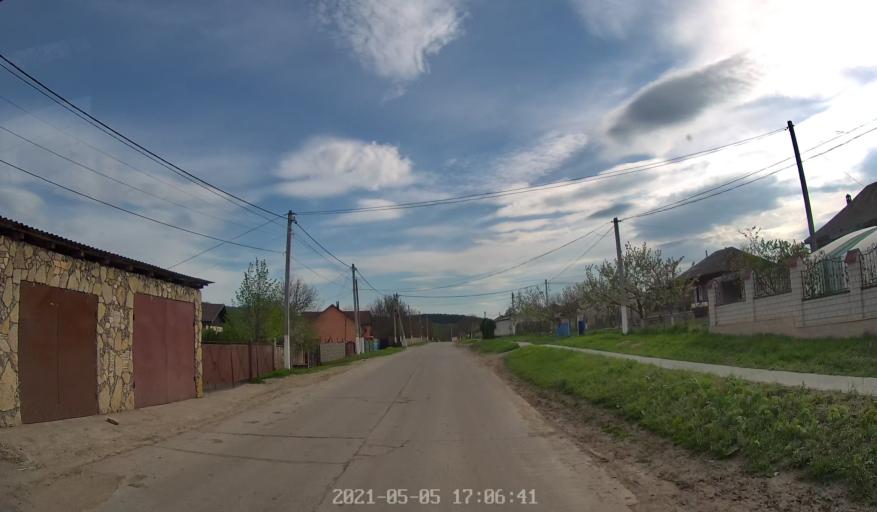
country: MD
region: Chisinau
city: Vadul lui Voda
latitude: 47.0184
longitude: 29.1385
